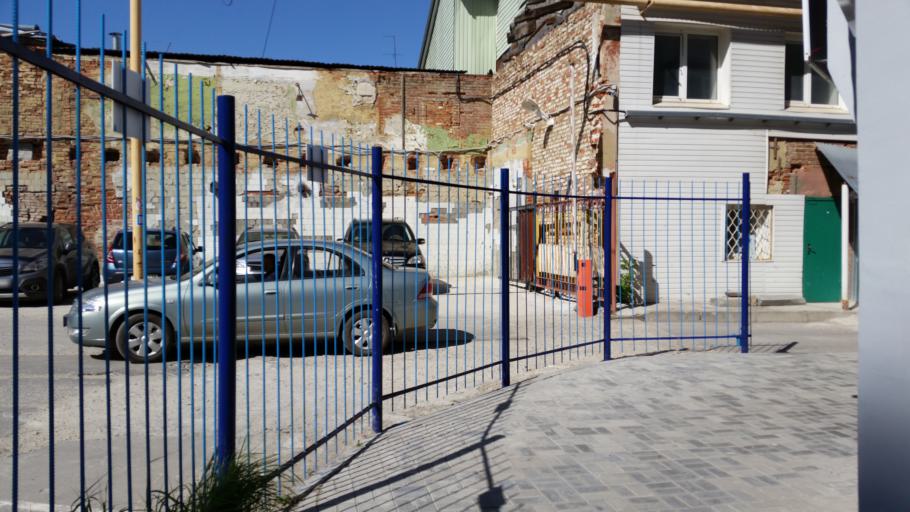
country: RU
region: Saratov
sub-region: Saratovskiy Rayon
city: Saratov
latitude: 51.5313
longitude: 46.0330
